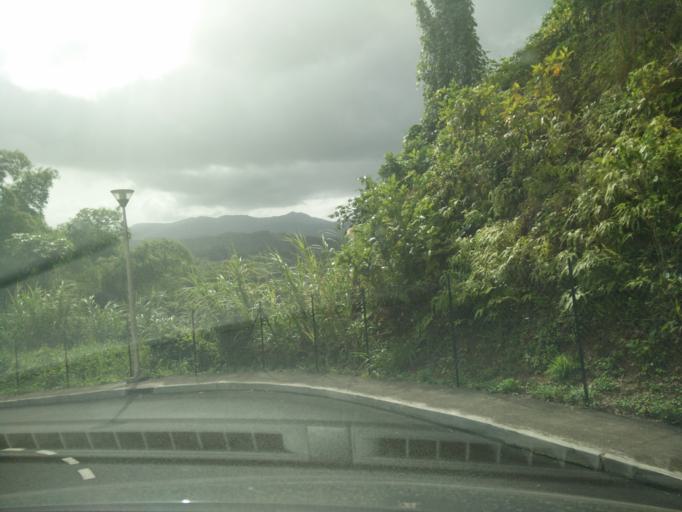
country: GP
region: Guadeloupe
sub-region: Guadeloupe
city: Petit-Bourg
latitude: 16.1944
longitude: -61.6564
